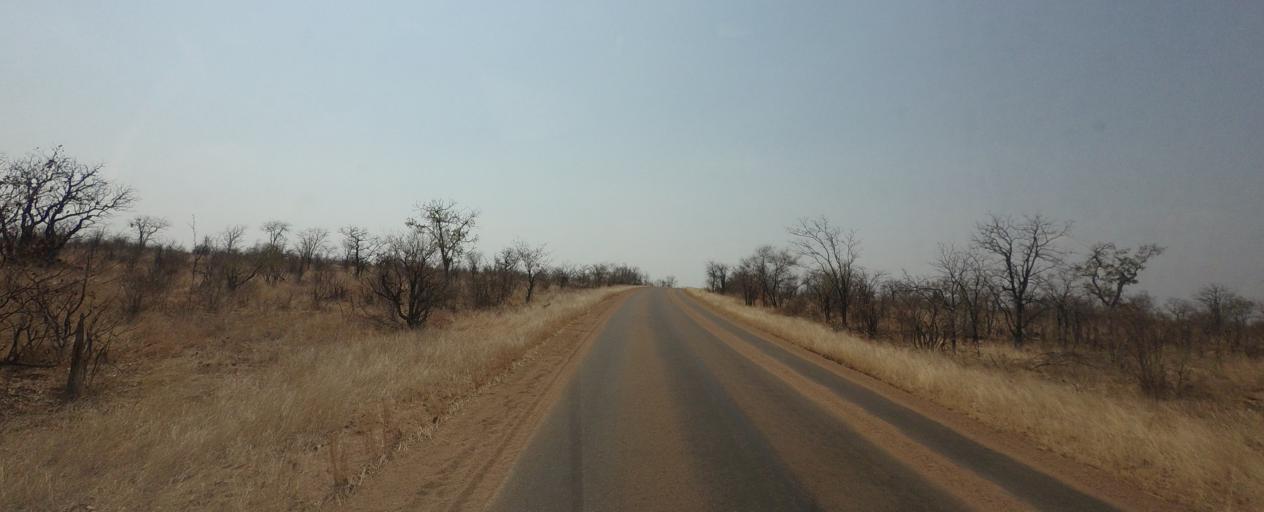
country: ZA
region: Limpopo
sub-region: Mopani District Municipality
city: Giyani
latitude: -23.2067
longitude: 31.3086
